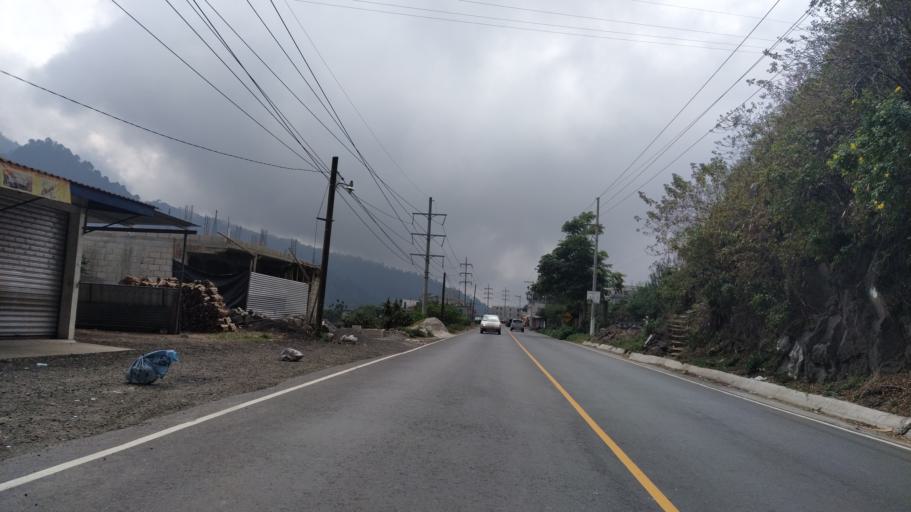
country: GT
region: Quetzaltenango
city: Zunil
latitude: 14.7511
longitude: -91.5098
